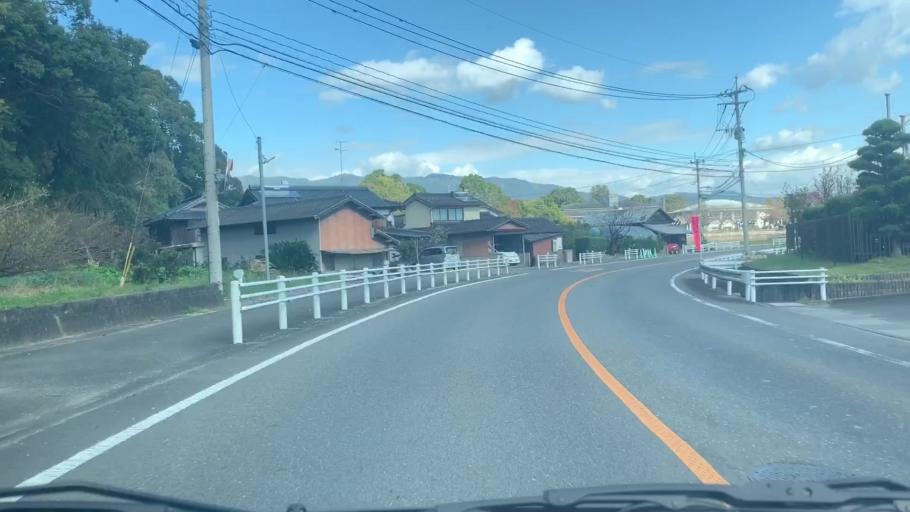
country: JP
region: Saga Prefecture
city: Saga-shi
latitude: 33.2703
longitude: 130.1808
